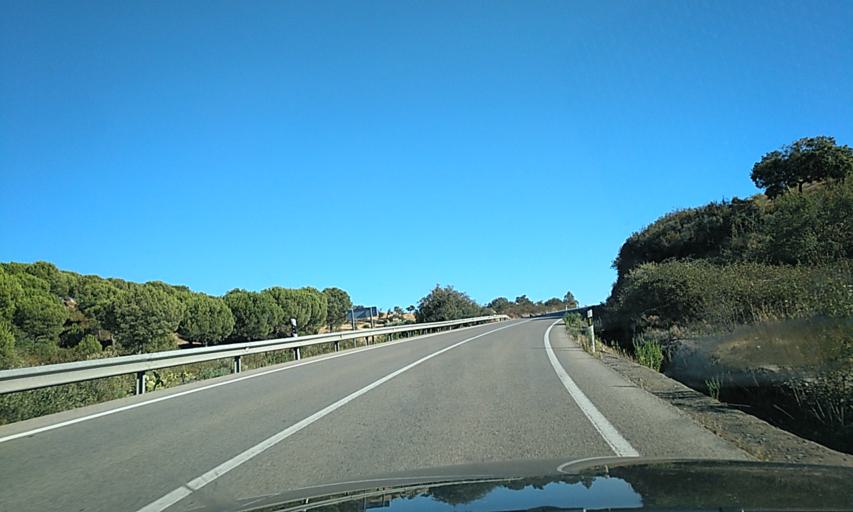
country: ES
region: Andalusia
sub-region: Provincia de Huelva
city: Santa Barbara de Casa
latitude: 37.8026
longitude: -7.1991
